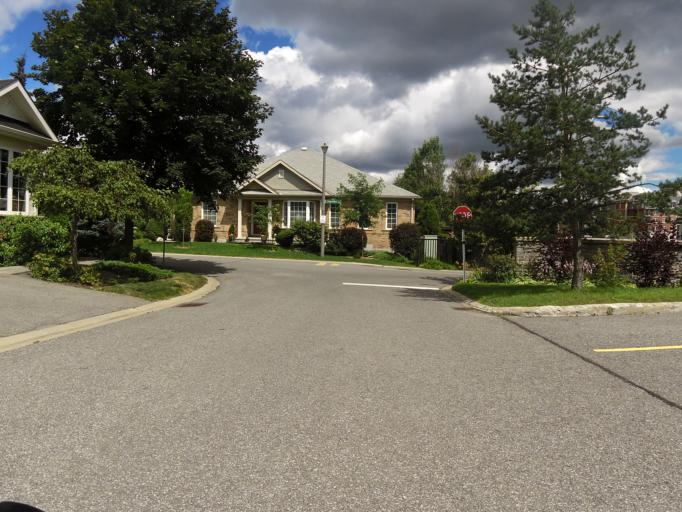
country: CA
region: Ontario
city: Bells Corners
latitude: 45.3163
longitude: -75.9038
